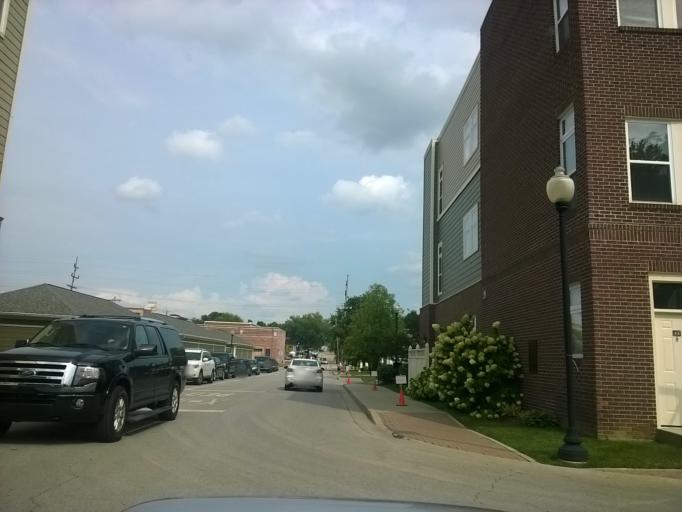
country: US
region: Indiana
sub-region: Hamilton County
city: Carmel
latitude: 39.9774
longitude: -86.1296
